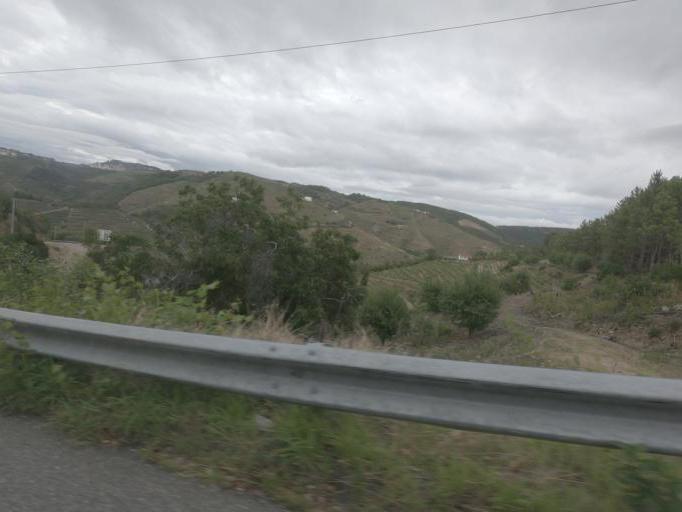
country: PT
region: Vila Real
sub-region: Sabrosa
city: Sabrosa
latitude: 41.2623
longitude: -7.5521
